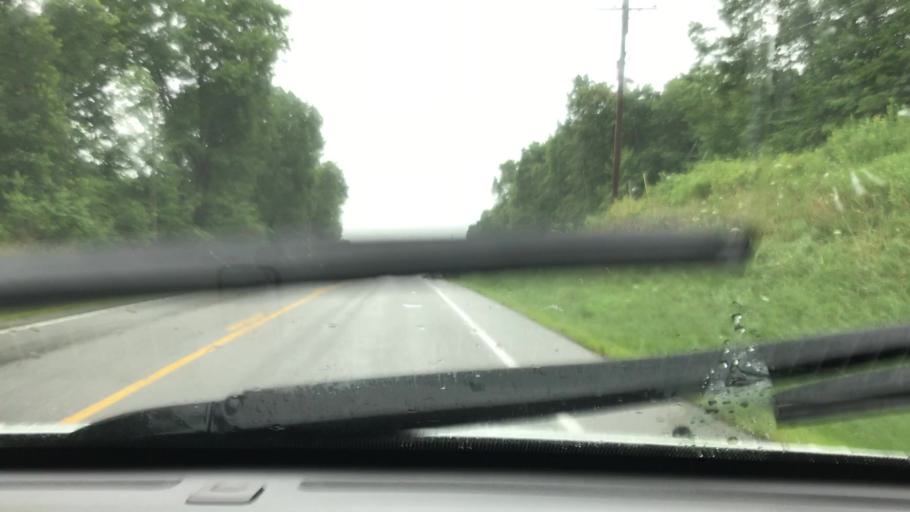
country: US
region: Pennsylvania
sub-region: Centre County
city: Philipsburg
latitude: 40.8503
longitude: -78.2195
